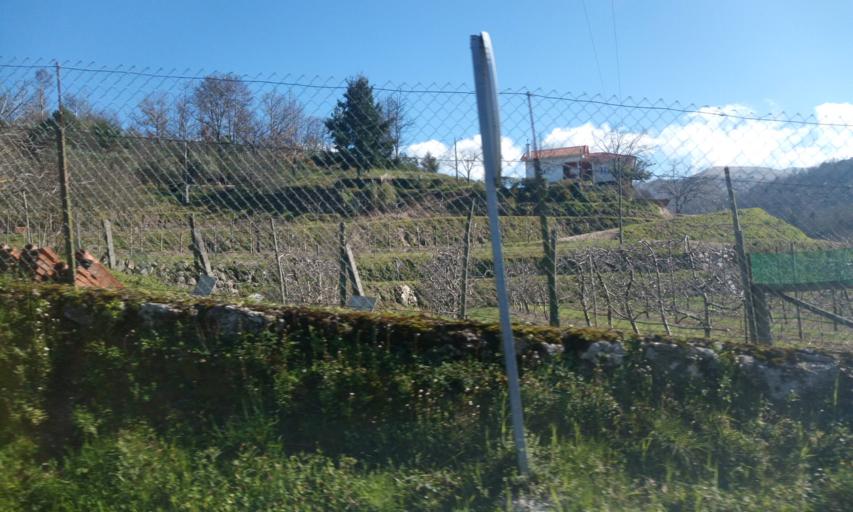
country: PT
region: Guarda
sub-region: Manteigas
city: Manteigas
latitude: 40.4773
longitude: -7.6183
